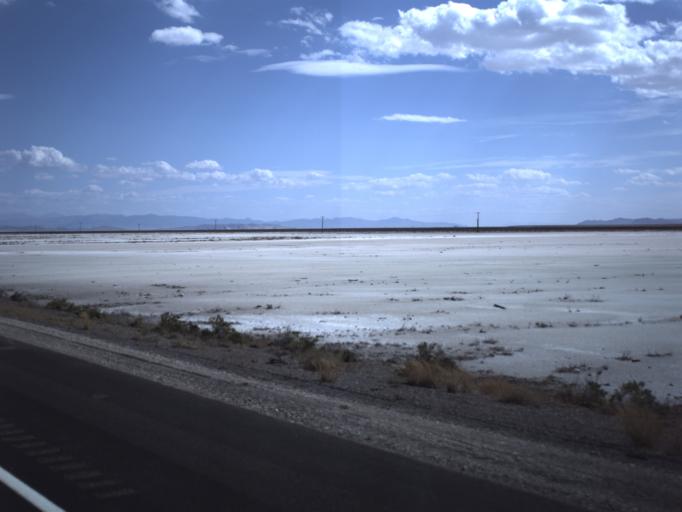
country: US
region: Utah
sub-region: Tooele County
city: Wendover
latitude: 40.7313
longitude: -113.5176
